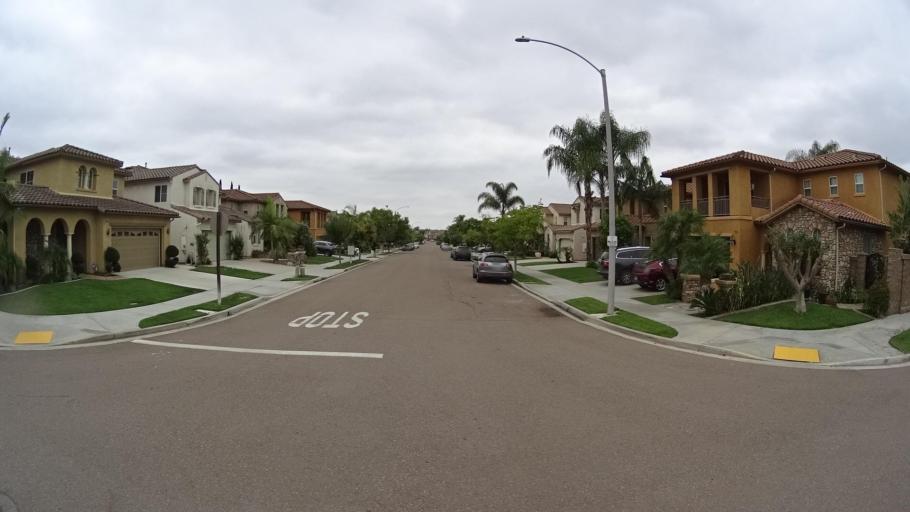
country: US
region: California
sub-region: San Diego County
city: Fairbanks Ranch
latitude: 33.0278
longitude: -117.1140
